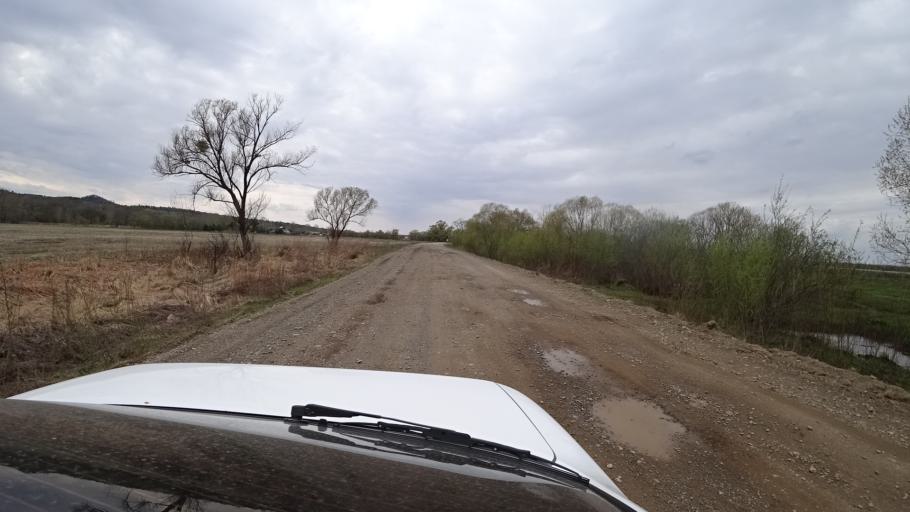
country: RU
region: Primorskiy
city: Novopokrovka
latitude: 45.4908
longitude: 134.4562
